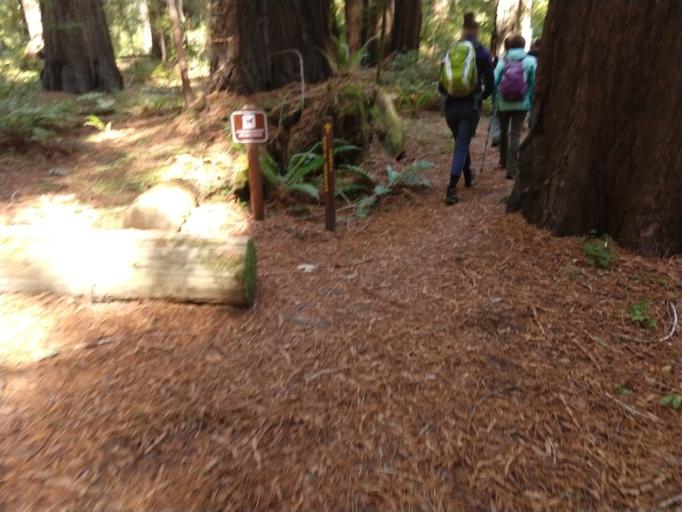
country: US
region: California
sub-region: Humboldt County
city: Rio Dell
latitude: 40.3522
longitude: -123.9925
